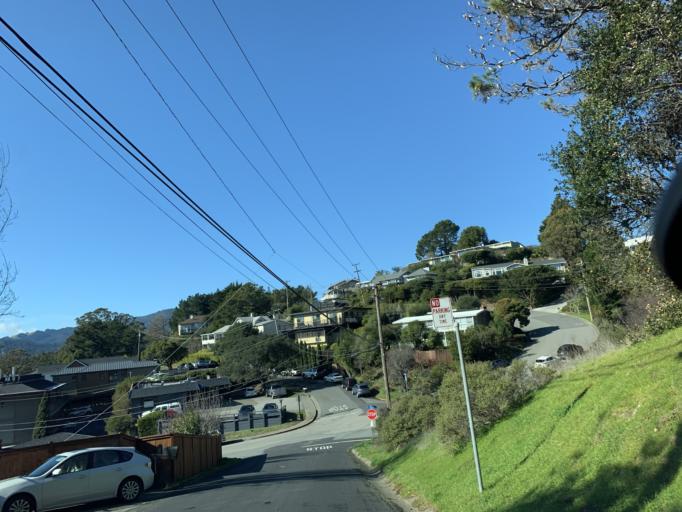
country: US
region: California
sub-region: Marin County
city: Strawberry
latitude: 37.9026
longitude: -122.5101
